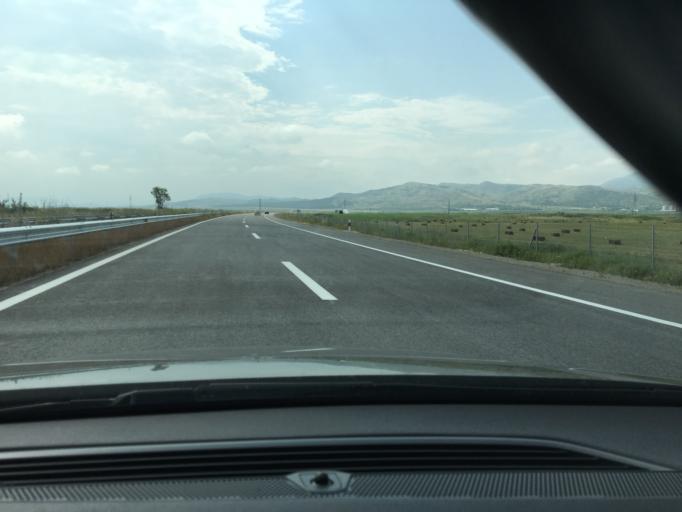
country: MK
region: Sveti Nikole
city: Sveti Nikole
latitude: 41.8268
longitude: 22.0060
